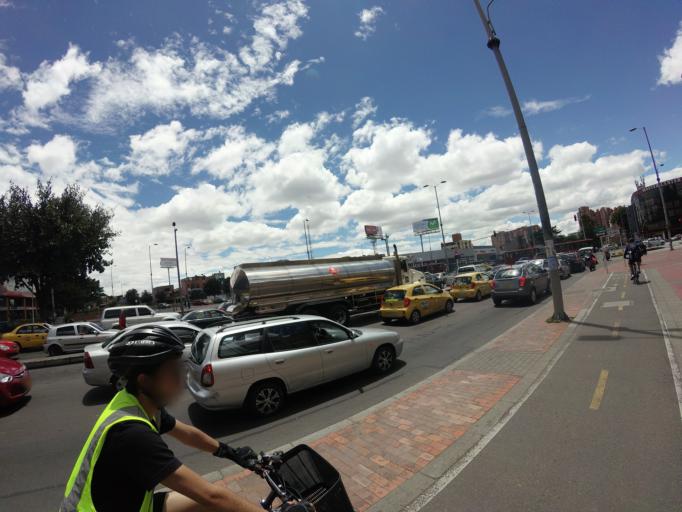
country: CO
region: Bogota D.C.
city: Barrio San Luis
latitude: 4.6891
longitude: -74.0646
